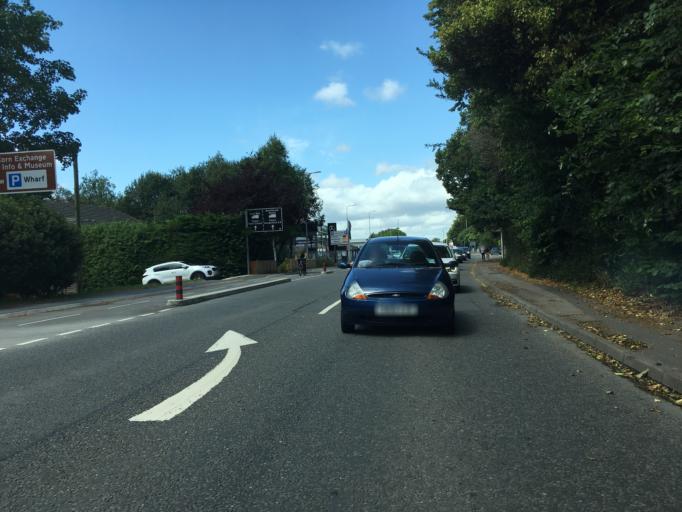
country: GB
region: England
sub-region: West Berkshire
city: Newbury
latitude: 51.4049
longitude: -1.3119
